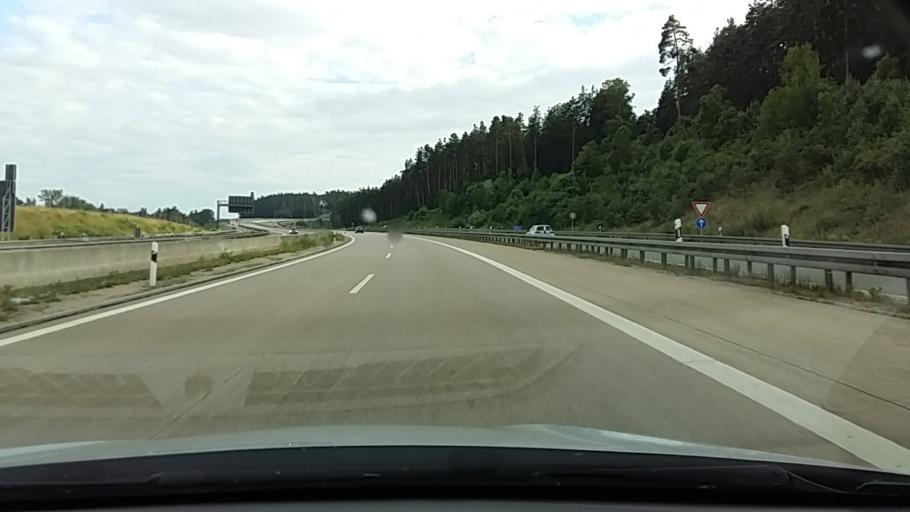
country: DE
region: Bavaria
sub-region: Upper Palatinate
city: Wernberg-Koblitz
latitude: 49.5167
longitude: 12.1625
